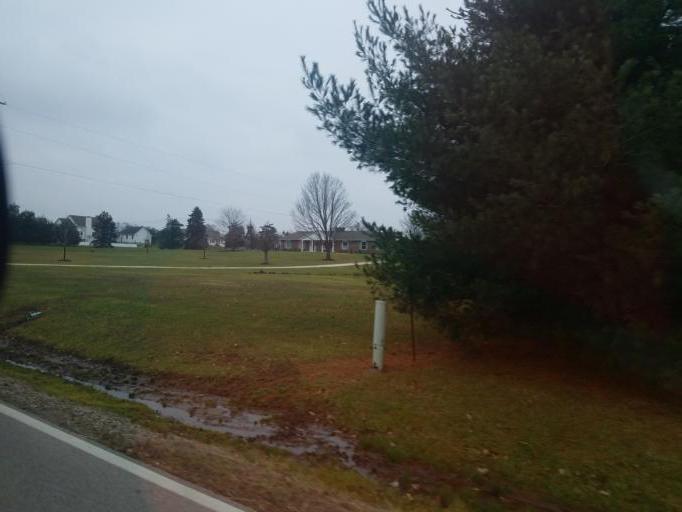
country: US
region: Ohio
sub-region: Delaware County
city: Sunbury
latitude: 40.2171
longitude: -82.9206
